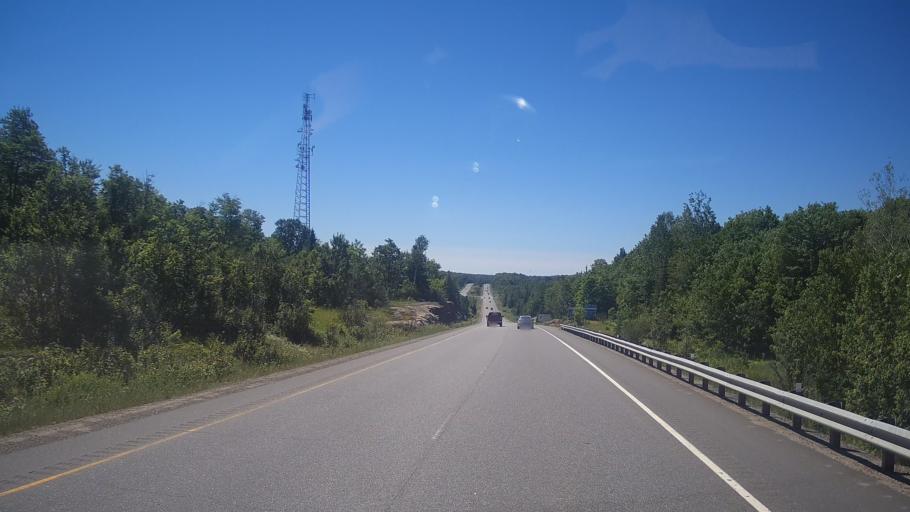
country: CA
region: Ontario
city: Huntsville
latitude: 45.2059
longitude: -79.3149
